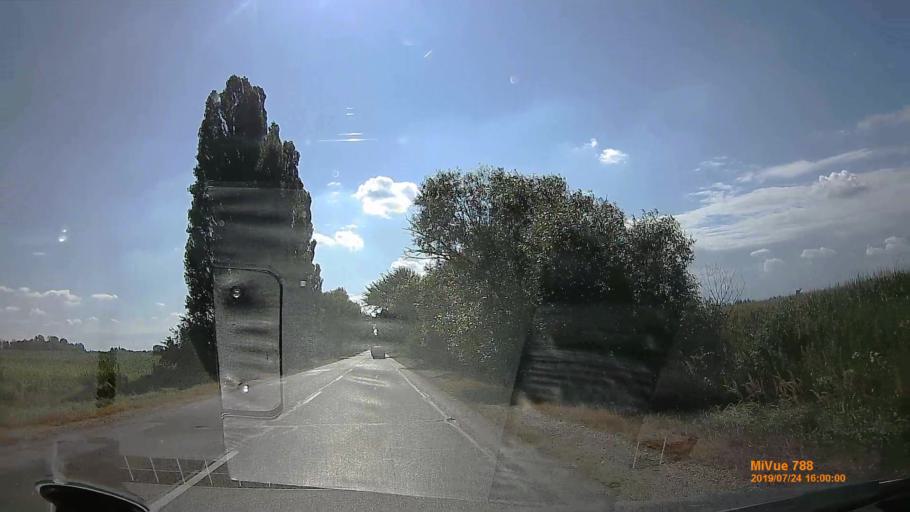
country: HU
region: Szabolcs-Szatmar-Bereg
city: Levelek
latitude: 47.9756
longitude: 22.0242
